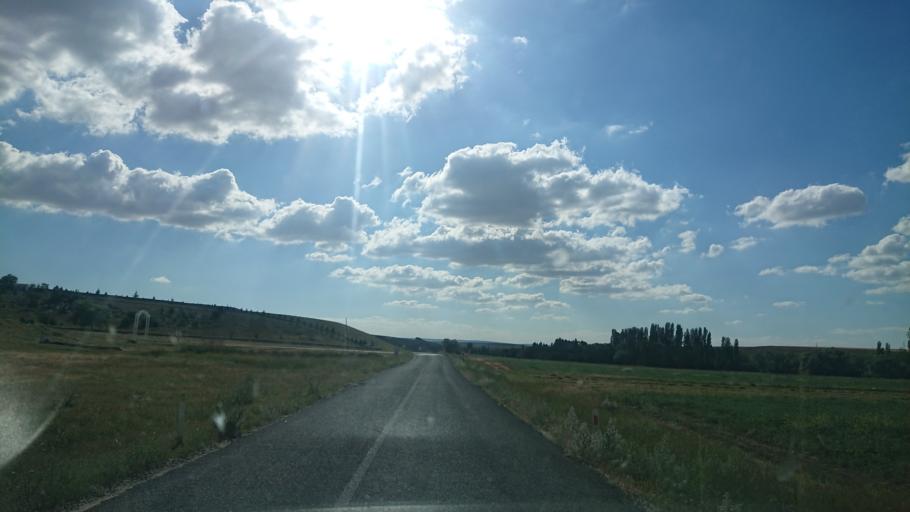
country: TR
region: Aksaray
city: Agacoren
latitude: 38.7562
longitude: 33.9161
